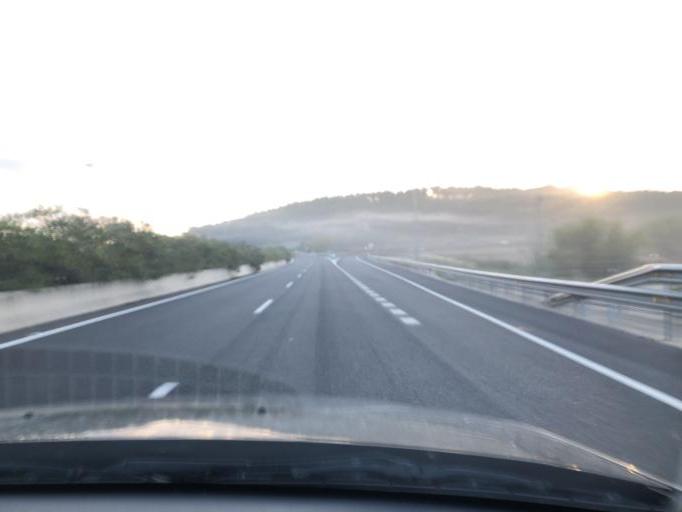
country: ES
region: Balearic Islands
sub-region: Illes Balears
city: Sant Joan
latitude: 39.5634
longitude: 3.0344
